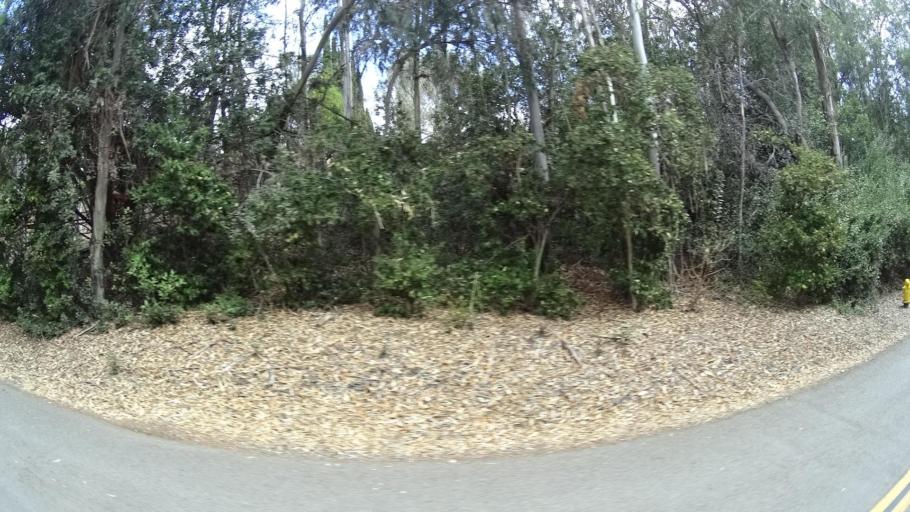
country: US
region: California
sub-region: San Diego County
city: Rancho Santa Fe
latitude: 33.0063
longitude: -117.2104
